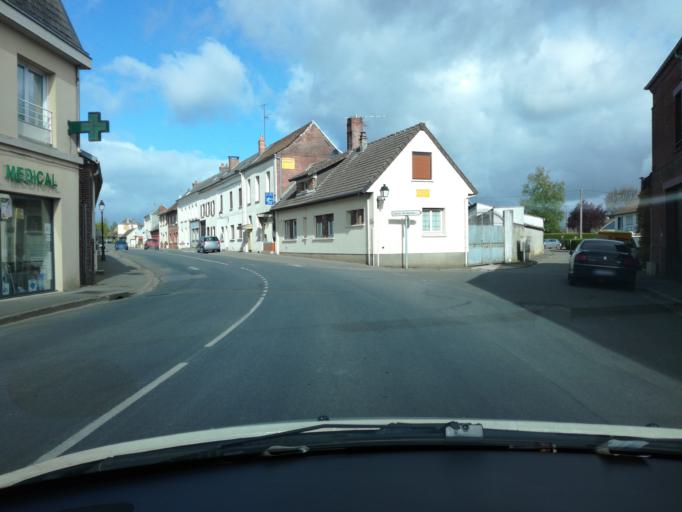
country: FR
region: Picardie
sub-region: Departement de la Somme
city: Hornoy-le-Bourg
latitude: 49.8470
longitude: 1.9014
